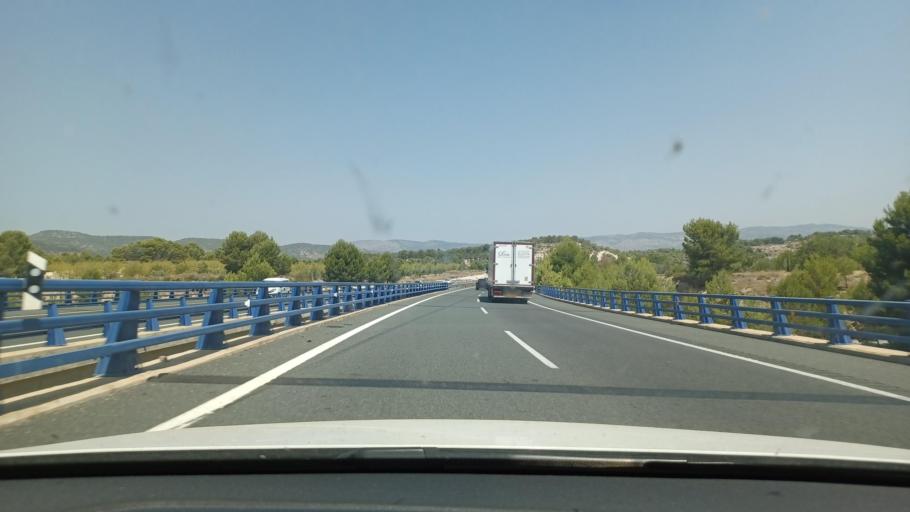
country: ES
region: Valencia
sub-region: Provincia de Alicante
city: Castalla
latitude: 38.5606
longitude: -0.6557
